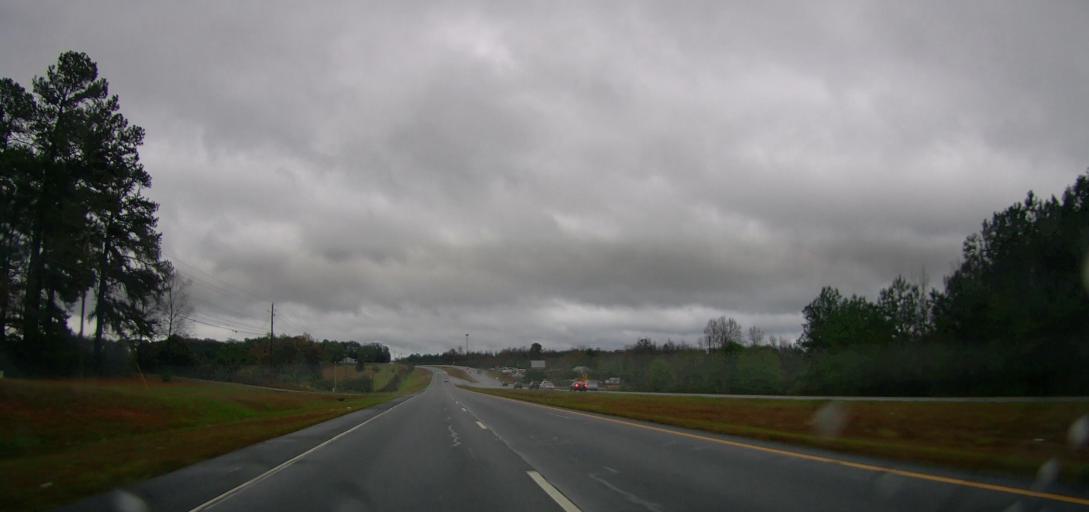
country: US
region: Georgia
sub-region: Jackson County
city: Commerce
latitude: 34.1609
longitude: -83.4441
